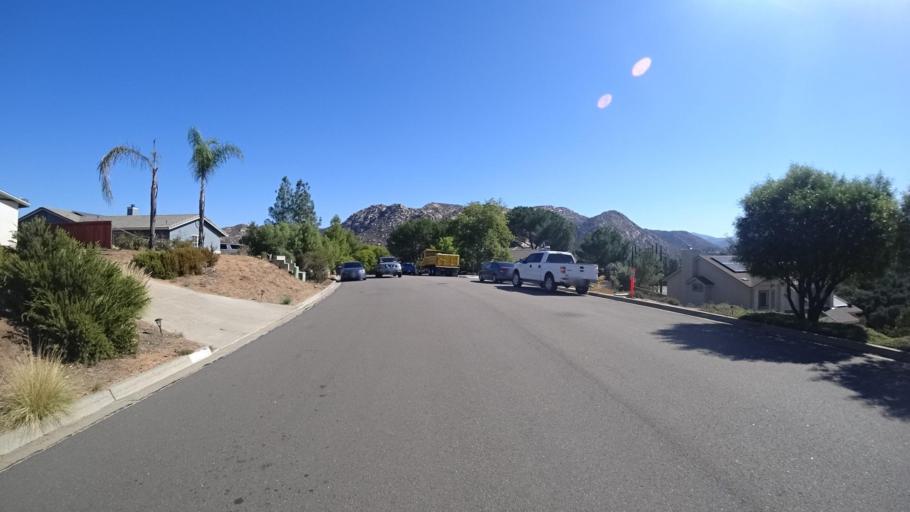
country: US
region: California
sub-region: San Diego County
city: San Diego Country Estates
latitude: 33.0053
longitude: -116.7942
